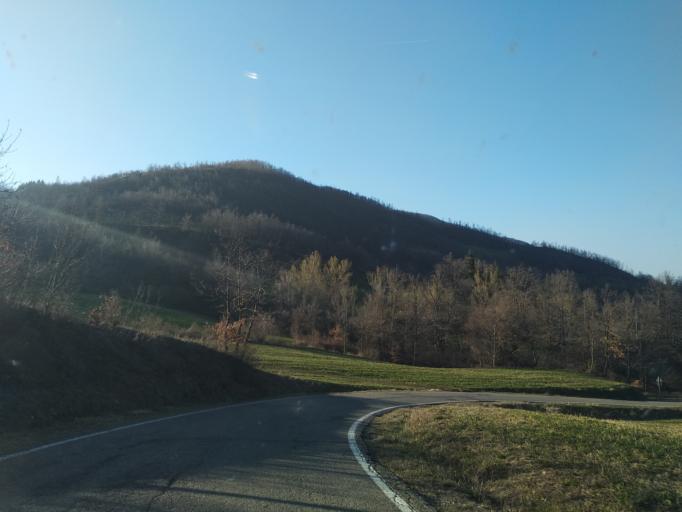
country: IT
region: Emilia-Romagna
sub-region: Provincia di Reggio Emilia
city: Ramiseto
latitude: 44.4100
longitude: 10.2697
